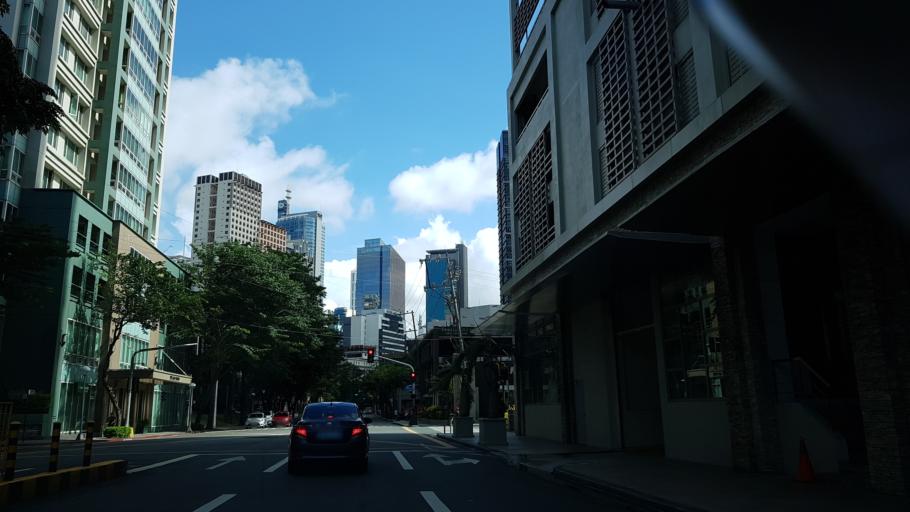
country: PH
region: Metro Manila
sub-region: Makati City
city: Makati City
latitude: 14.5513
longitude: 121.0192
